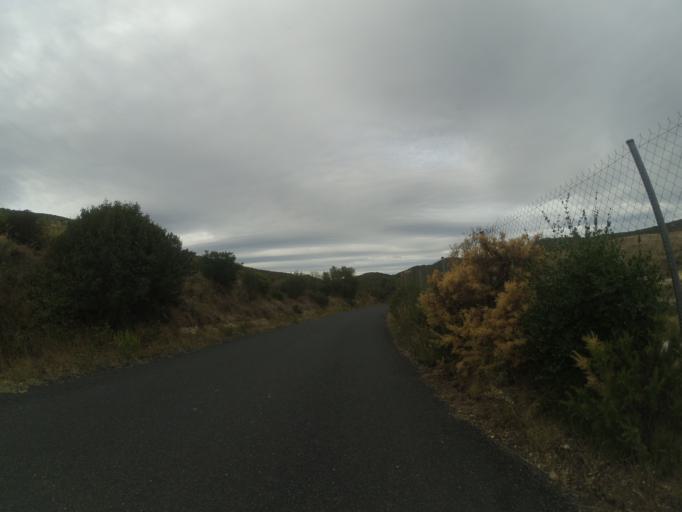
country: FR
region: Languedoc-Roussillon
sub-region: Departement des Pyrenees-Orientales
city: Corneilla-la-Riviere
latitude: 42.7283
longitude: 2.7397
